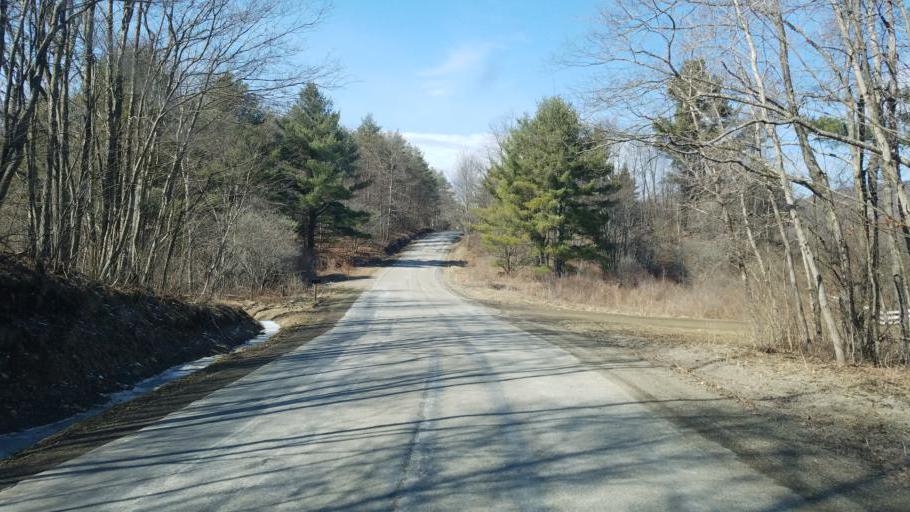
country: US
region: New York
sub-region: Allegany County
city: Andover
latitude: 41.9499
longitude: -77.8264
